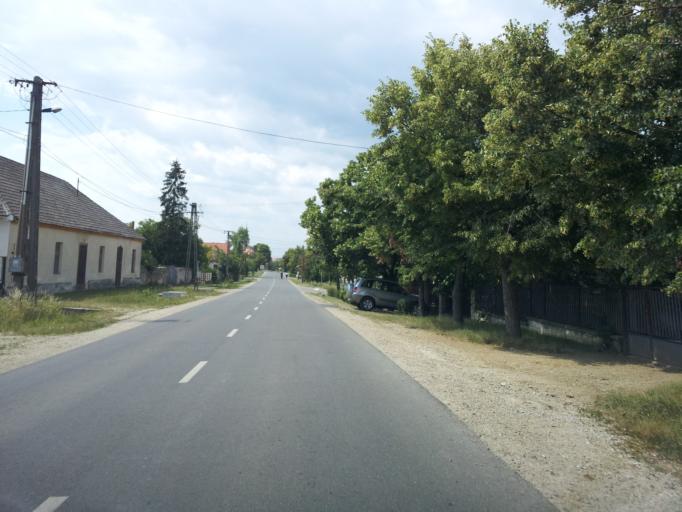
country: HU
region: Veszprem
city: Zanka
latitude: 46.9803
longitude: 17.7023
